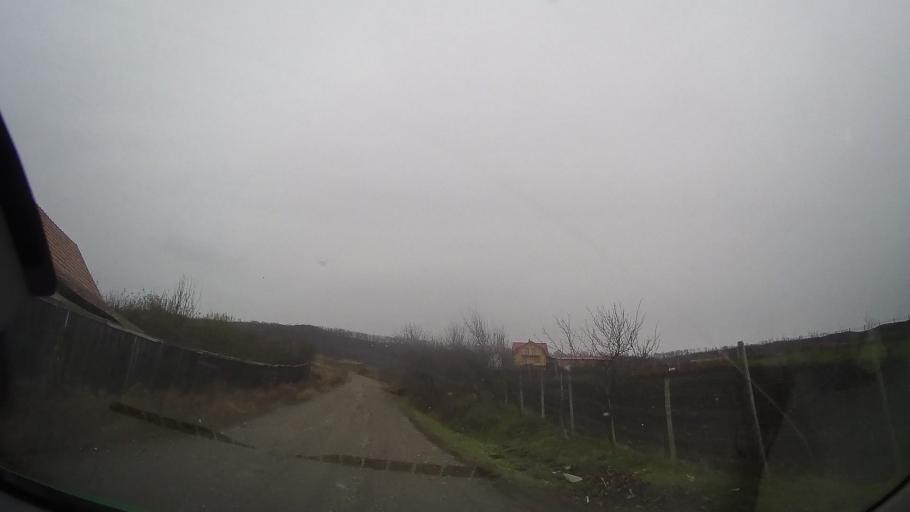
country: RO
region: Mures
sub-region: Comuna Ceausu de Campie
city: Ceausu de Campie
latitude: 46.6465
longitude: 24.4973
